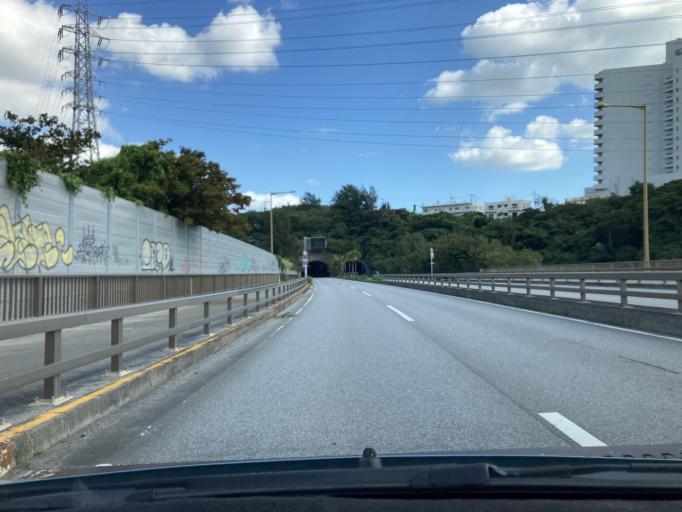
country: JP
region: Okinawa
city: Okinawa
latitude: 26.3152
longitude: 127.8087
